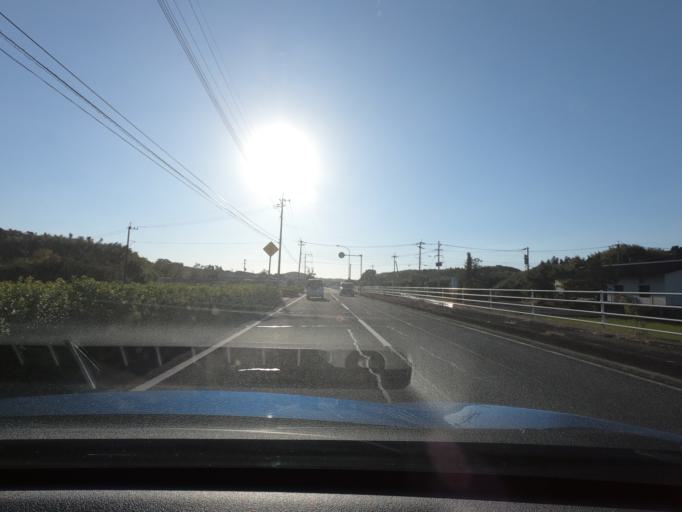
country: JP
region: Kagoshima
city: Akune
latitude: 32.0697
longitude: 130.2416
